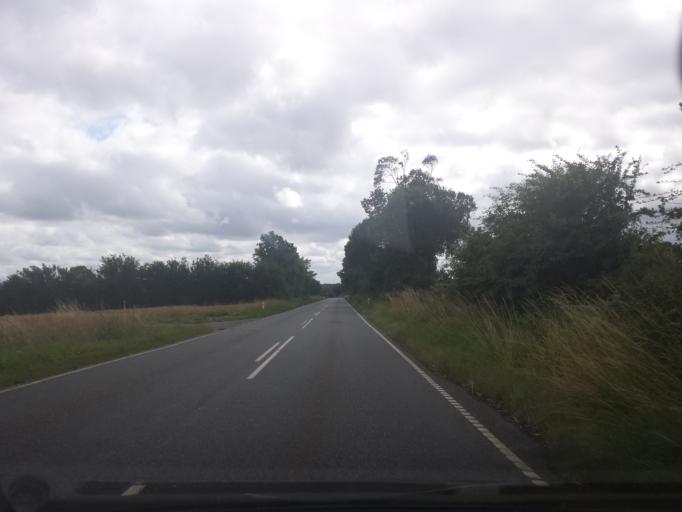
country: DK
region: South Denmark
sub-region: Sonderborg Kommune
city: Grasten
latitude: 54.9439
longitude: 9.6310
